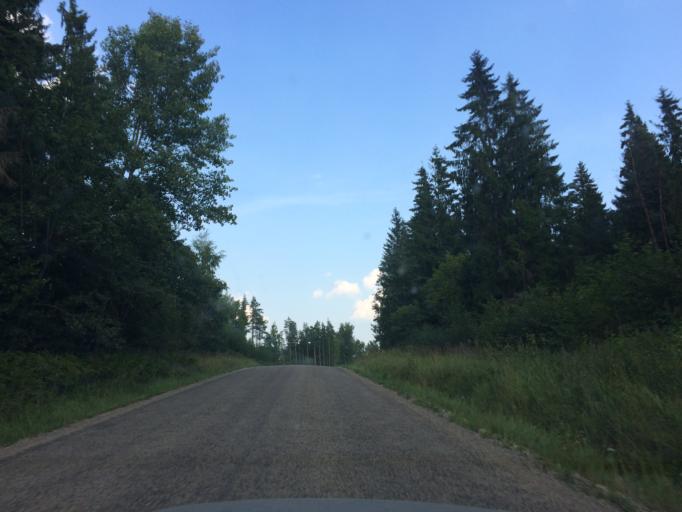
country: LV
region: Rezekne
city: Rezekne
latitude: 56.5722
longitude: 27.4767
